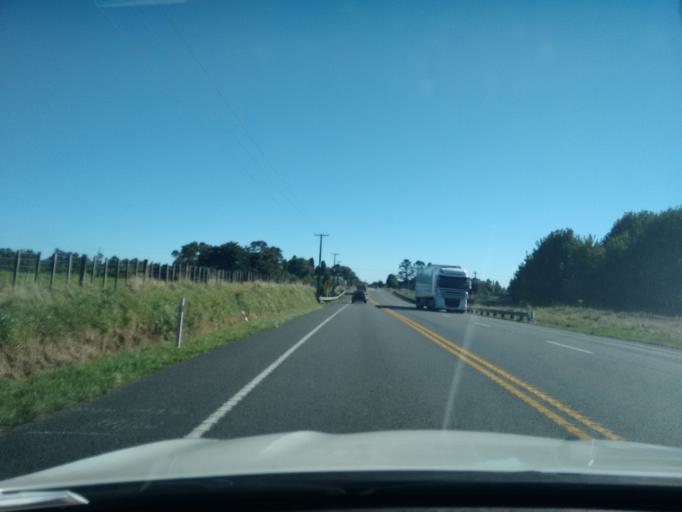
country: NZ
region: Taranaki
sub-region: New Plymouth District
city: New Plymouth
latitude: -39.2026
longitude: 174.2301
